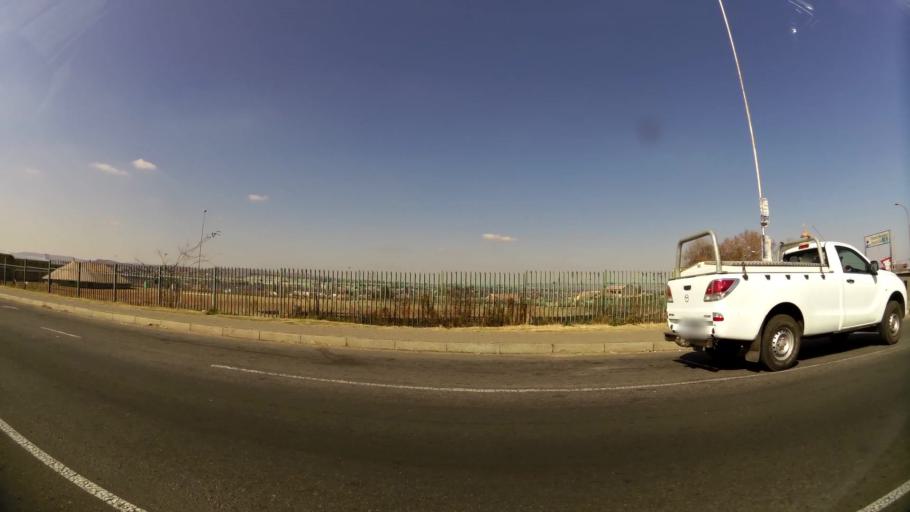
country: ZA
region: Gauteng
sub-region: City of Johannesburg Metropolitan Municipality
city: Soweto
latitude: -26.2733
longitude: 27.8729
